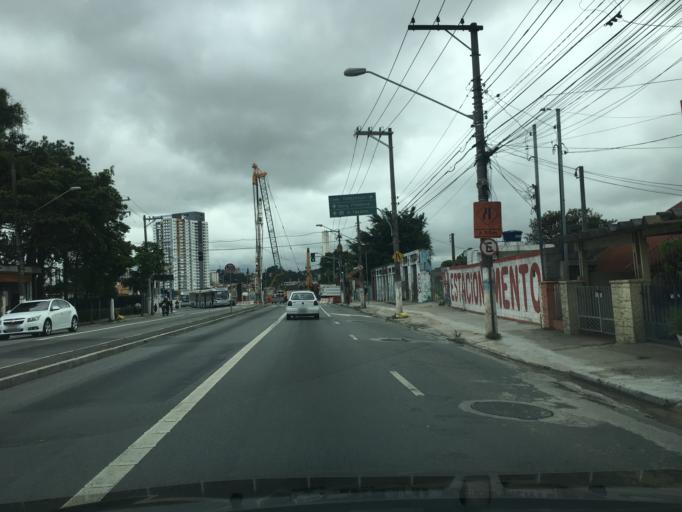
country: BR
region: Sao Paulo
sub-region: Taboao Da Serra
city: Taboao da Serra
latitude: -23.5972
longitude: -46.7402
